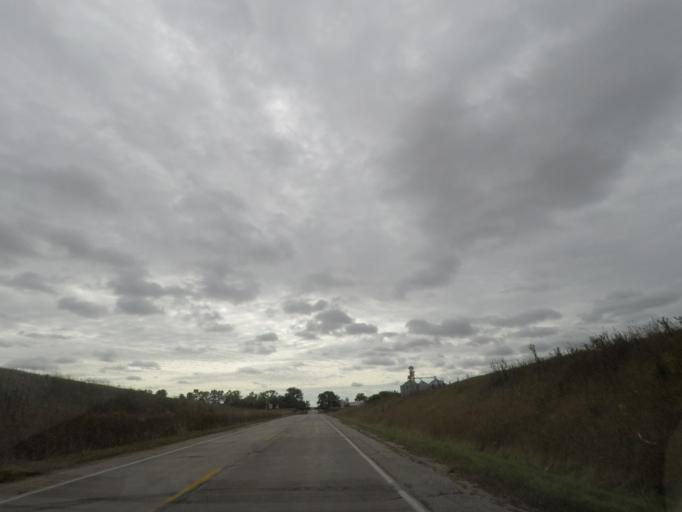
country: US
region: Iowa
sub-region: Story County
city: Nevada
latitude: 42.0220
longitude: -93.3095
